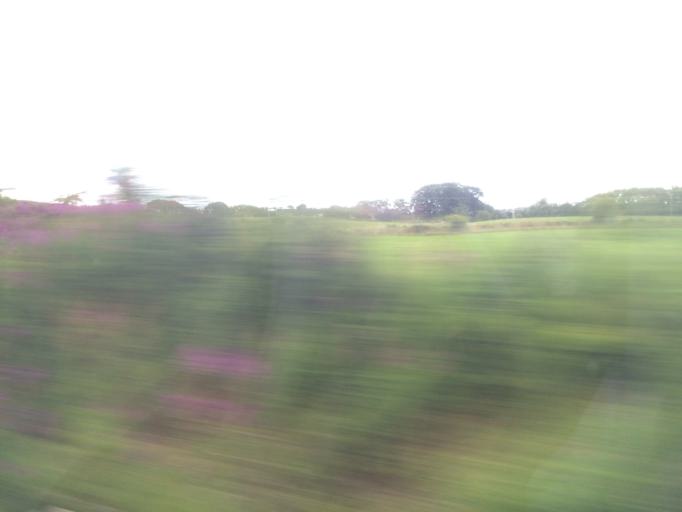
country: GB
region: Scotland
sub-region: Falkirk
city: Bonnybridge
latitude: 55.9876
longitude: -3.9077
